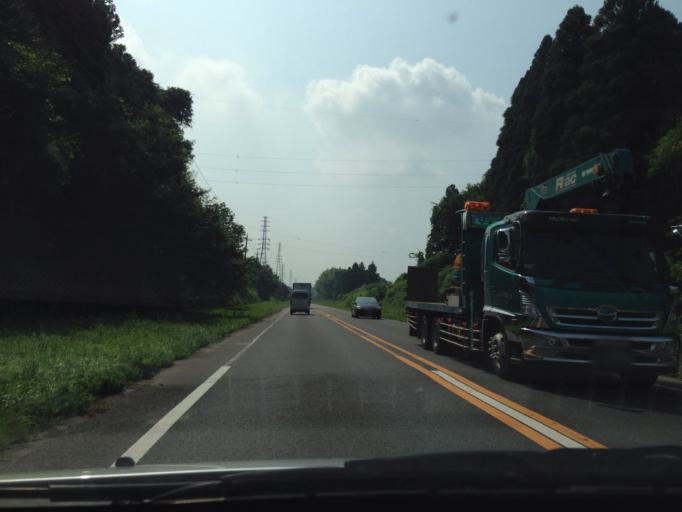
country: JP
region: Ibaraki
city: Ami
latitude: 36.0300
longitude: 140.2299
